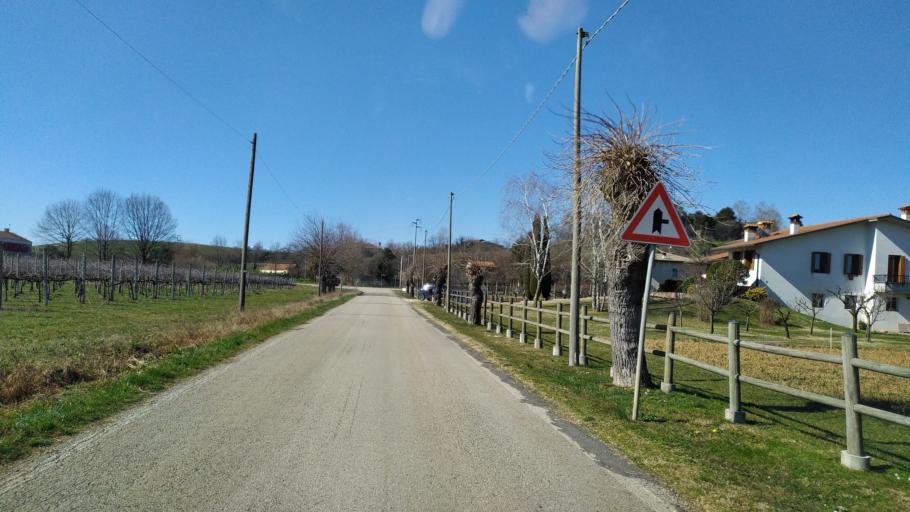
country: IT
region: Veneto
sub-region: Provincia di Vicenza
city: Mason Vicentino
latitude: 45.7030
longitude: 11.5930
